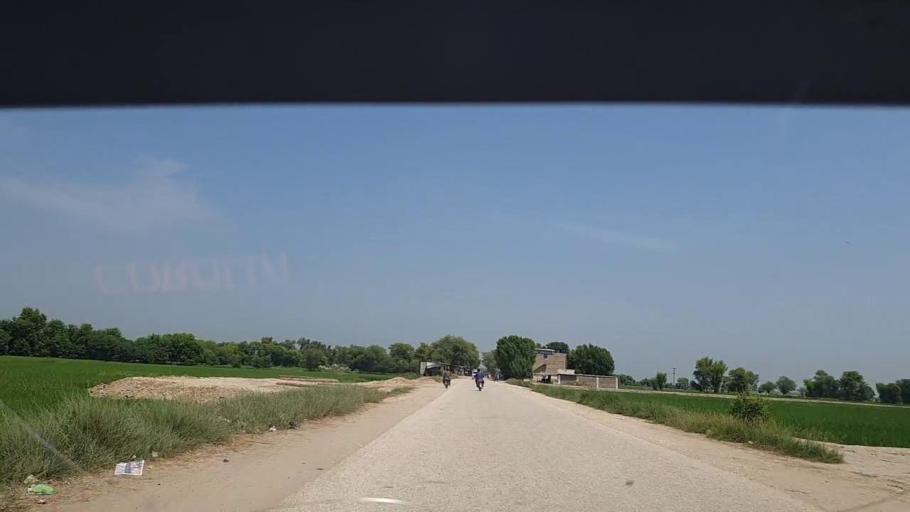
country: PK
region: Sindh
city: Rustam jo Goth
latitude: 28.0819
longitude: 68.7865
